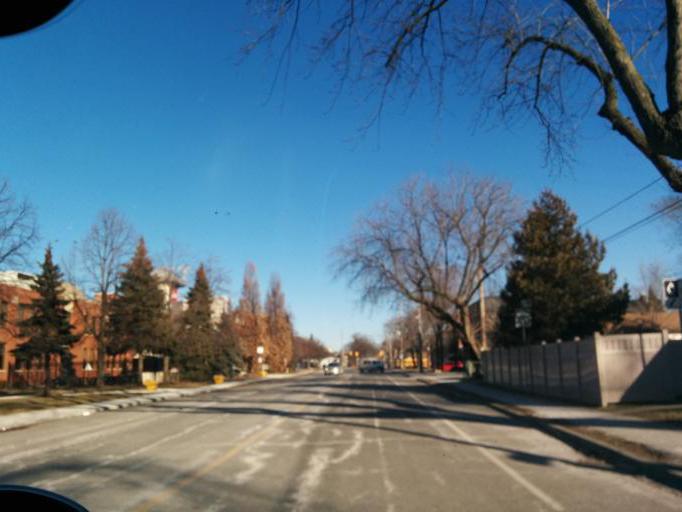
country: CA
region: Ontario
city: Etobicoke
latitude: 43.6044
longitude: -79.5018
